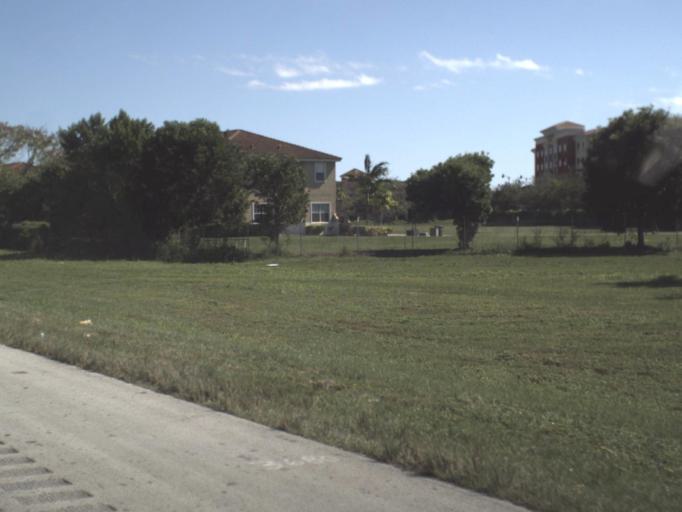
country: US
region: Florida
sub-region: Miami-Dade County
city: Leisure City
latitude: 25.4793
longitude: -80.4364
